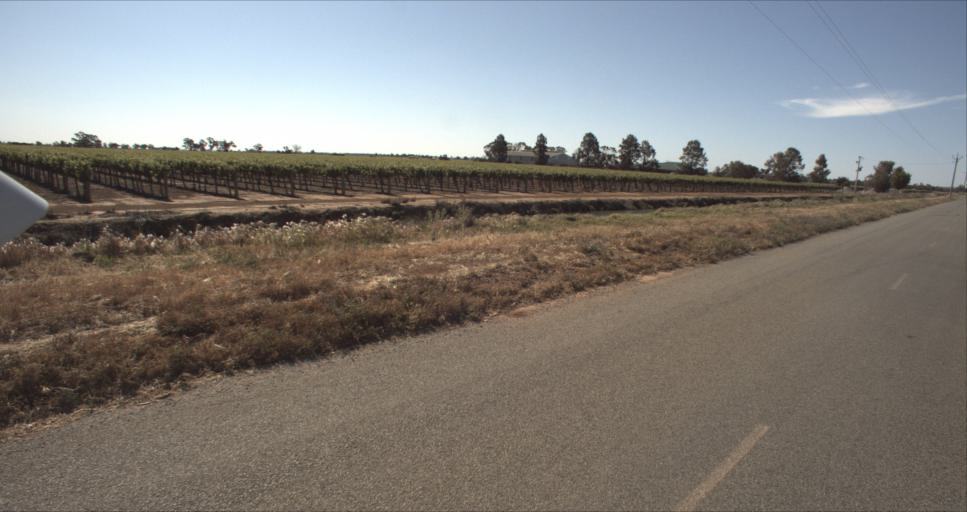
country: AU
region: New South Wales
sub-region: Leeton
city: Leeton
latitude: -34.5830
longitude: 146.3795
